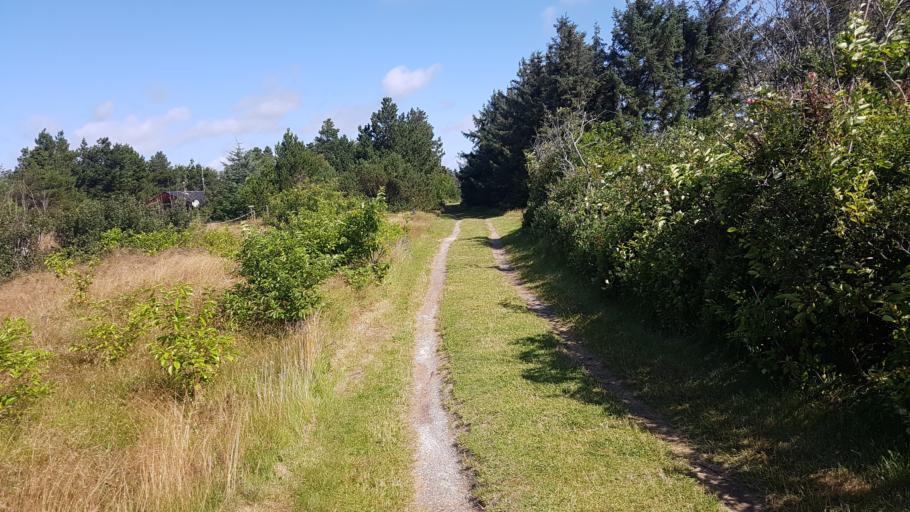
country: DE
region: Schleswig-Holstein
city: List
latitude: 55.1267
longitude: 8.5392
